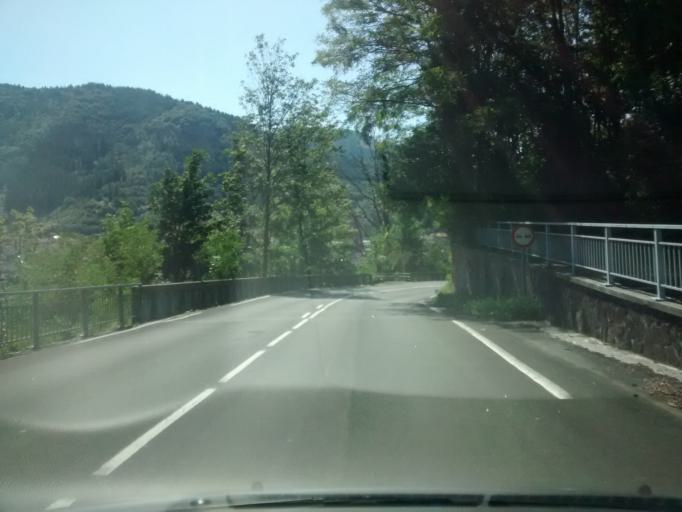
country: ES
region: Basque Country
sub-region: Provincia de Guipuzcoa
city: Eibar
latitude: 43.1878
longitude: -2.4690
